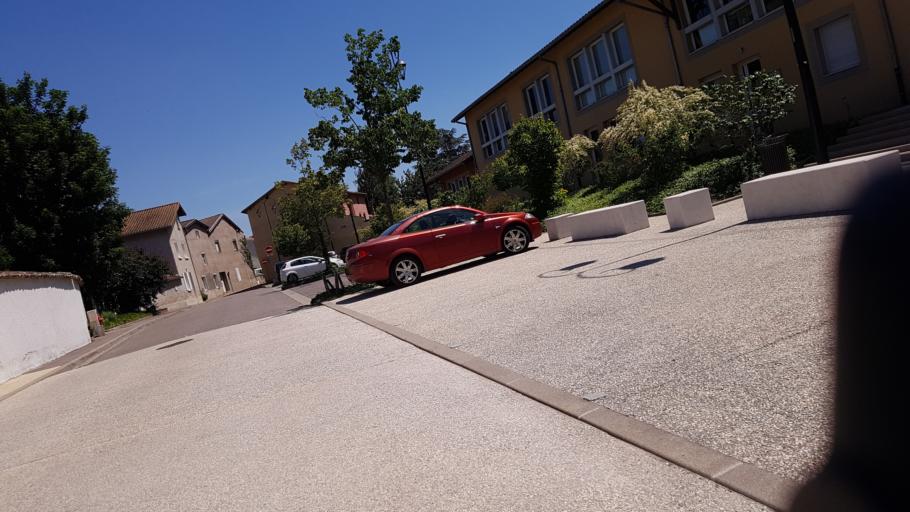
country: FR
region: Rhone-Alpes
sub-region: Departement du Rhone
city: Sathonay-Village
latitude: 45.8326
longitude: 4.8792
